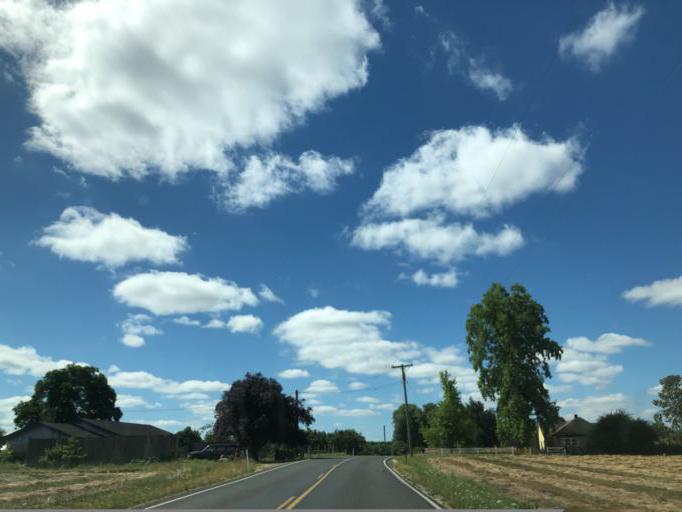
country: US
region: Oregon
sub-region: Marion County
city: Mount Angel
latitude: 45.1116
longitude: -122.7278
